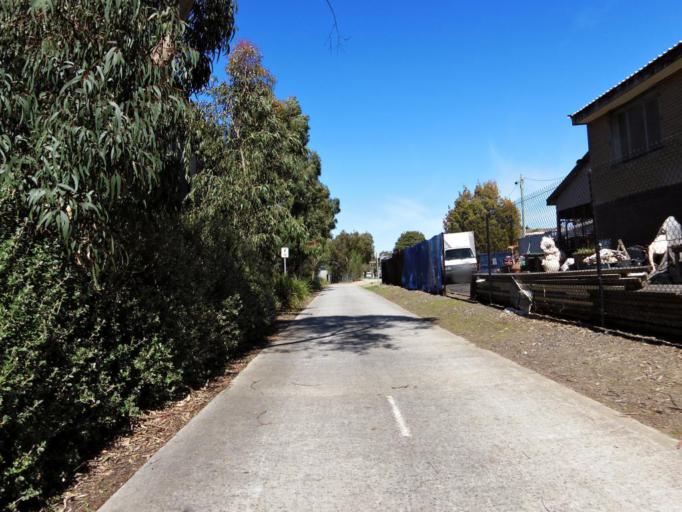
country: AU
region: Victoria
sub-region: Greater Dandenong
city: Dandenong
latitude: -37.9709
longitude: 145.1939
